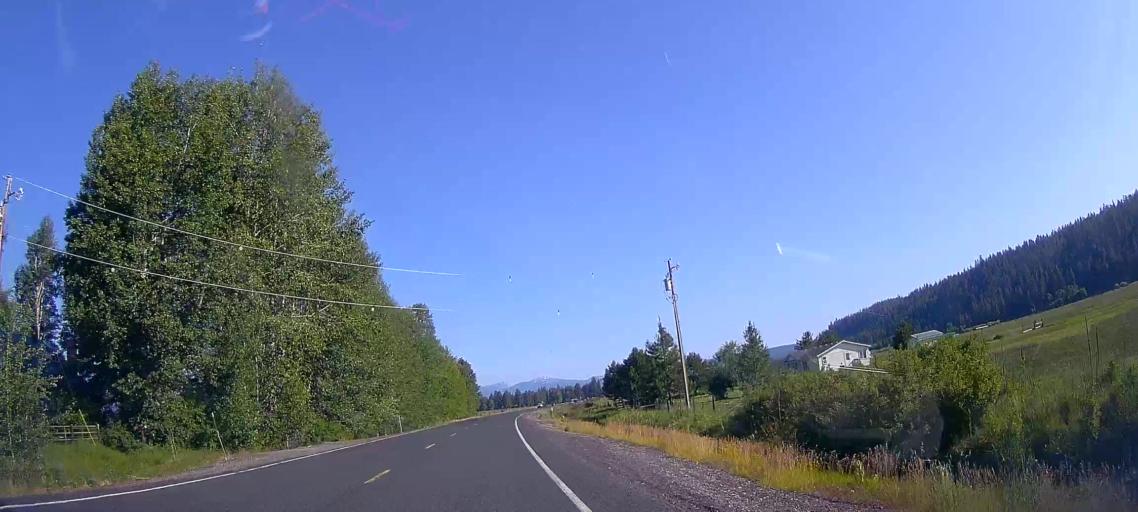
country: US
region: Oregon
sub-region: Klamath County
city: Klamath Falls
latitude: 42.6639
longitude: -121.9649
